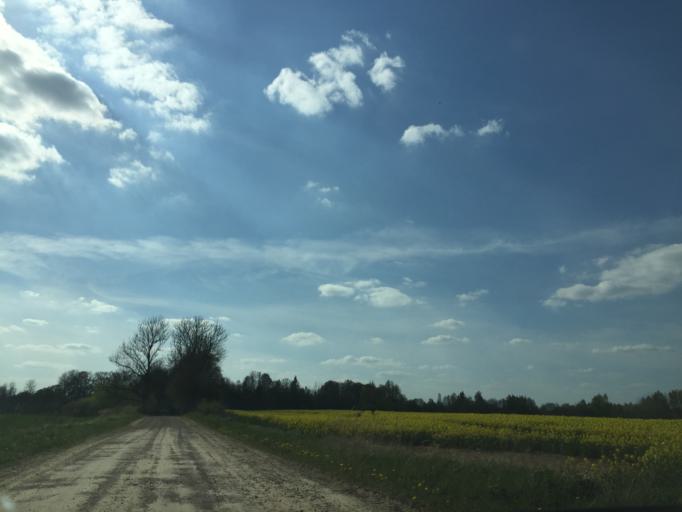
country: LV
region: Lecava
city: Iecava
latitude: 56.5105
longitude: 24.3286
